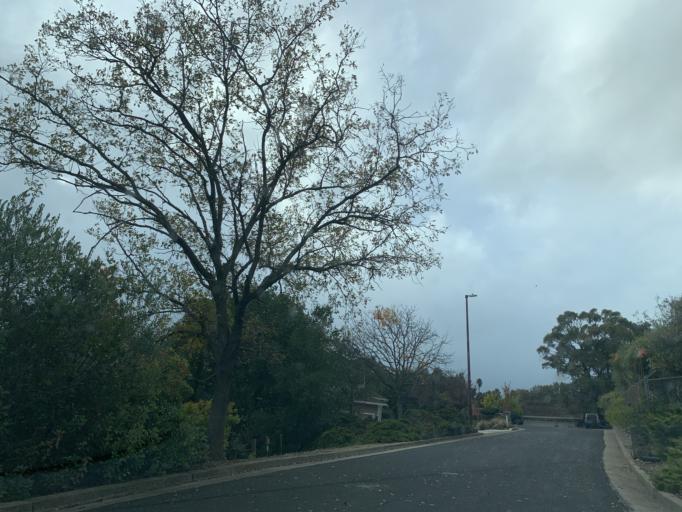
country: US
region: California
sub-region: Santa Clara County
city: Monte Sereno
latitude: 37.2537
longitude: -121.9834
